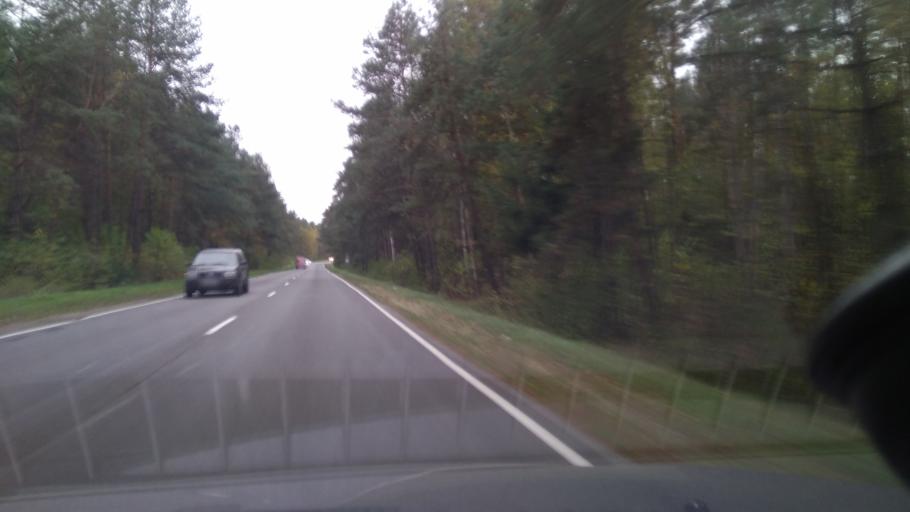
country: BY
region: Minsk
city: Druzhny
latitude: 53.6361
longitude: 27.8959
